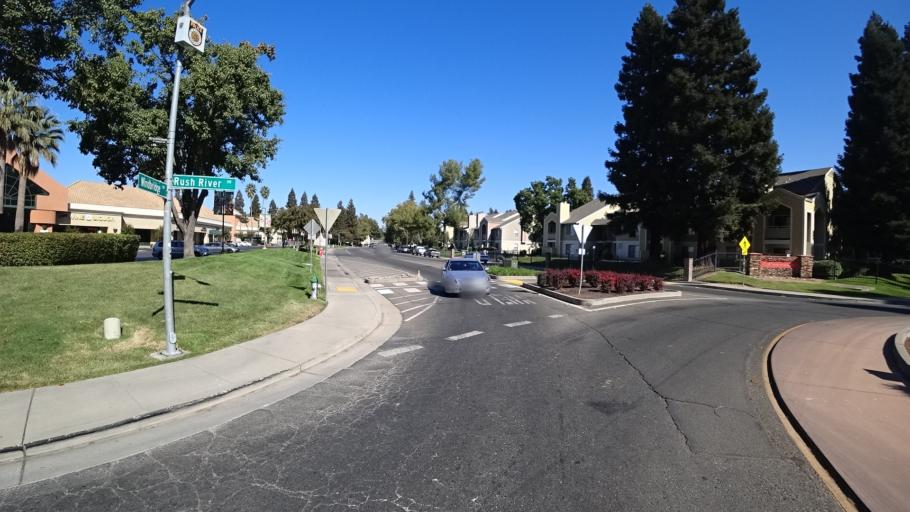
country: US
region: California
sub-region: Sacramento County
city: Parkway
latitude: 38.4848
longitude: -121.5338
